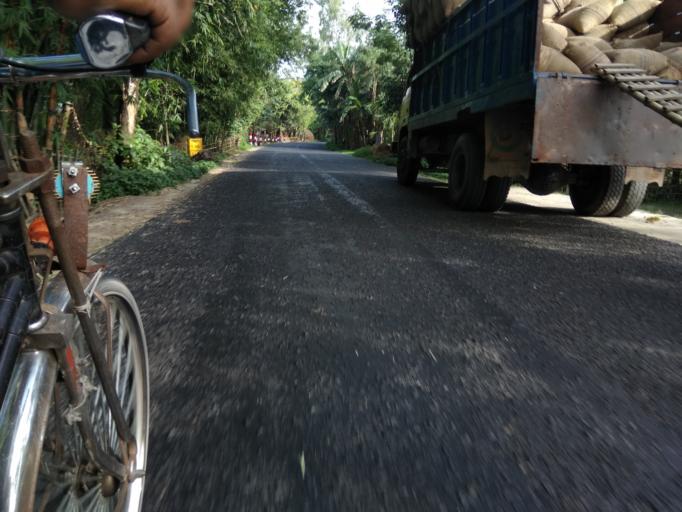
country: BD
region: Rangpur Division
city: Rangpur
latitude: 25.8410
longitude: 89.1134
